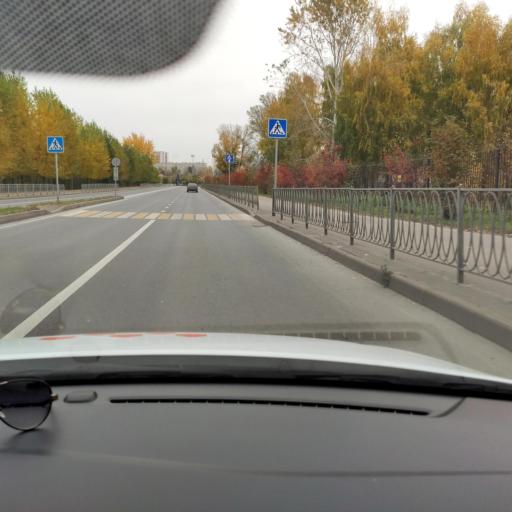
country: RU
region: Tatarstan
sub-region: Gorod Kazan'
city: Kazan
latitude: 55.7570
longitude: 49.1496
